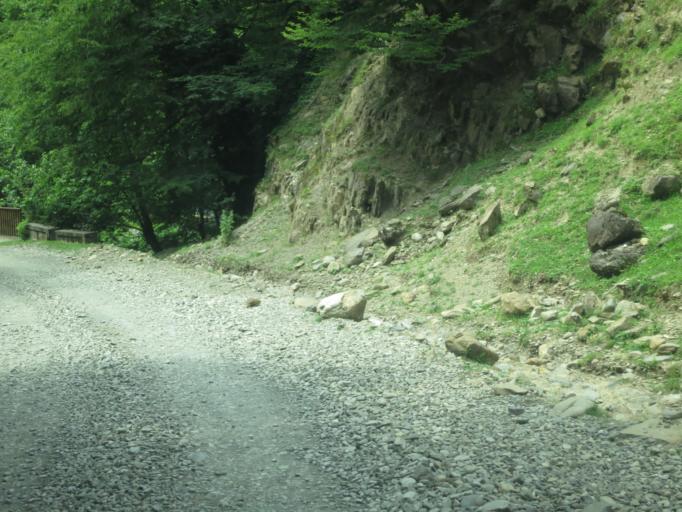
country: GE
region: Kakheti
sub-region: Telavi
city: Telavi
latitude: 42.1804
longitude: 45.4368
